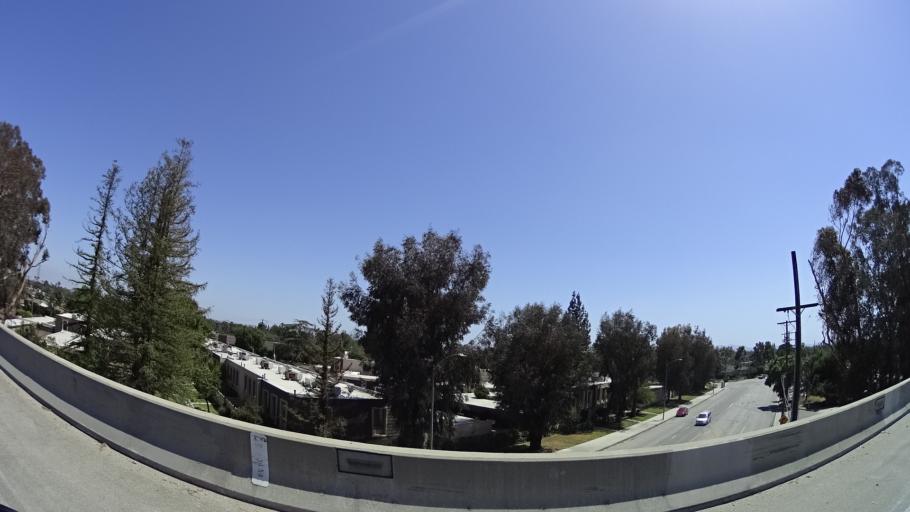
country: US
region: California
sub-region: Los Angeles County
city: San Fernando
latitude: 34.2657
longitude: -118.4602
